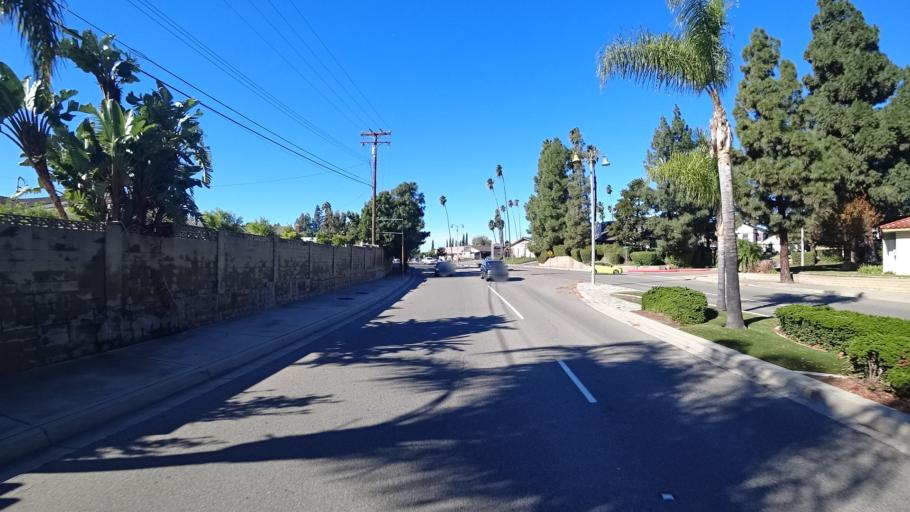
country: US
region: California
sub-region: Orange County
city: Placentia
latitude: 33.8890
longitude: -117.8464
